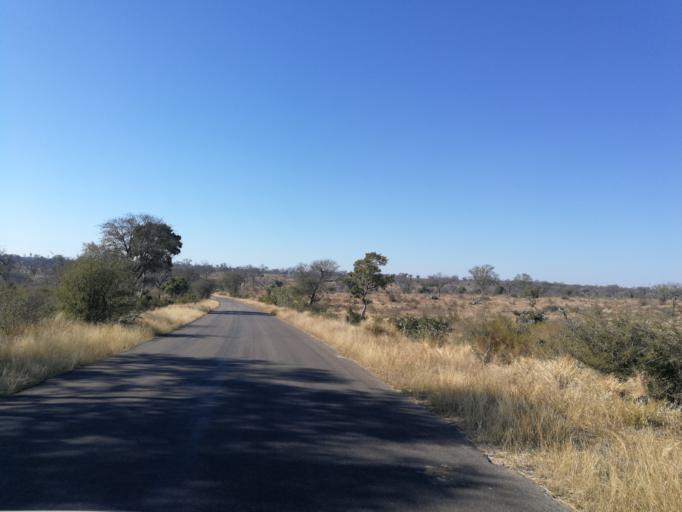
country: ZA
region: Limpopo
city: Thulamahashi
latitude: -24.9931
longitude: 31.5188
